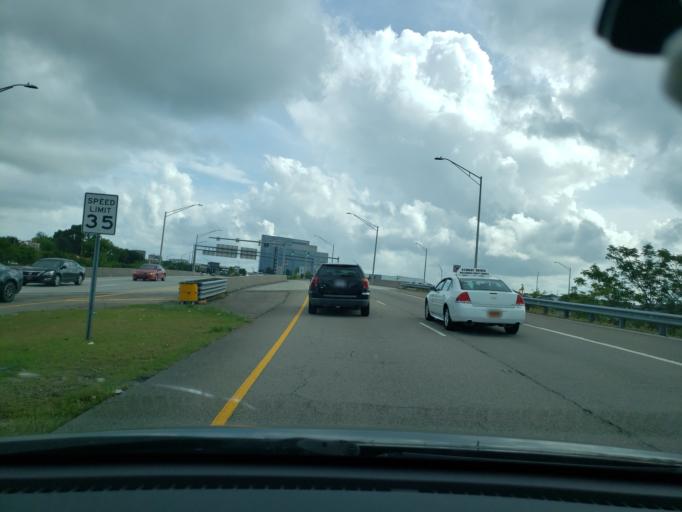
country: US
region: North Carolina
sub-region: New Hanover County
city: Wilmington
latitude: 34.2517
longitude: -77.9470
